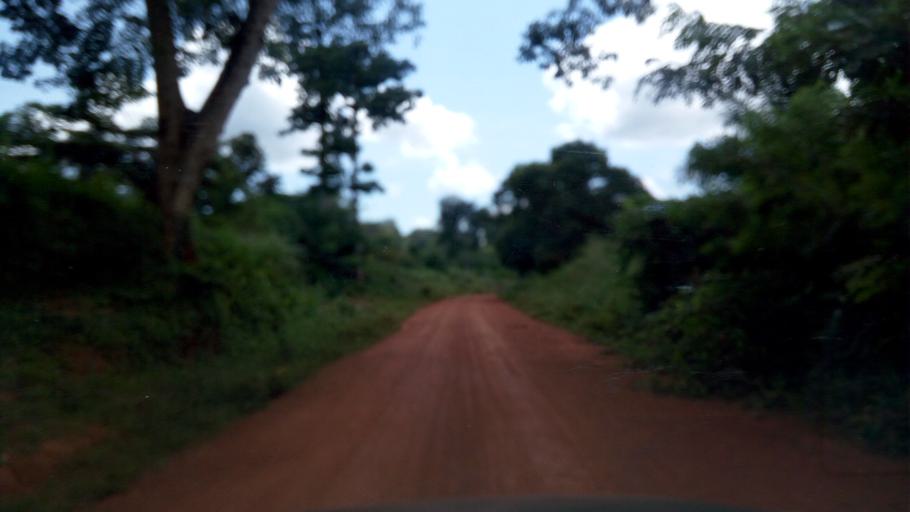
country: CF
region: Bangui
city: Bangui
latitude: 4.2165
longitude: 18.6930
